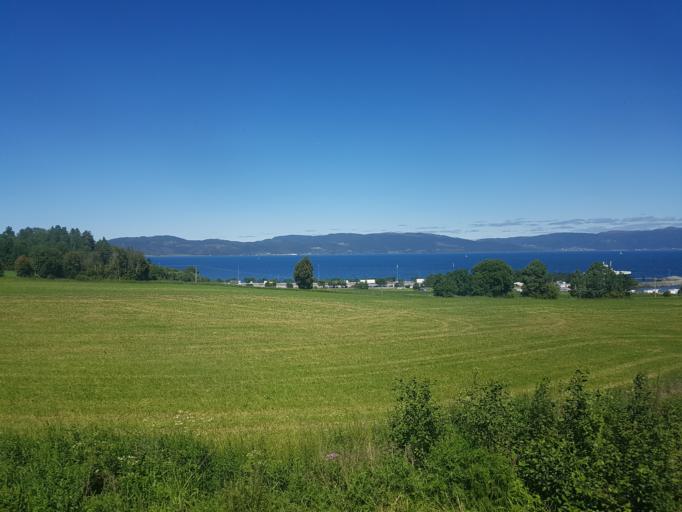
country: NO
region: Sor-Trondelag
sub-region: Melhus
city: Melhus
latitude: 63.4461
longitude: 10.2014
